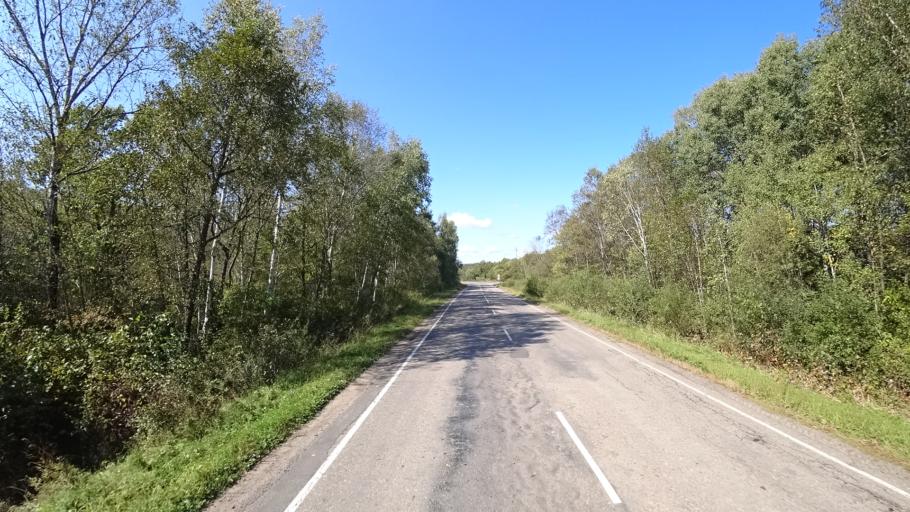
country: RU
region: Amur
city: Arkhara
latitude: 49.4048
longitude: 130.1270
